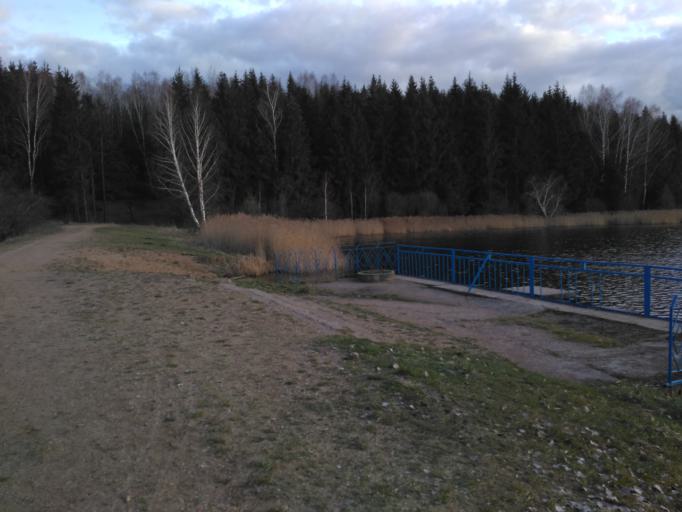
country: BY
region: Minsk
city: Slabada
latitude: 54.0491
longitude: 27.8665
